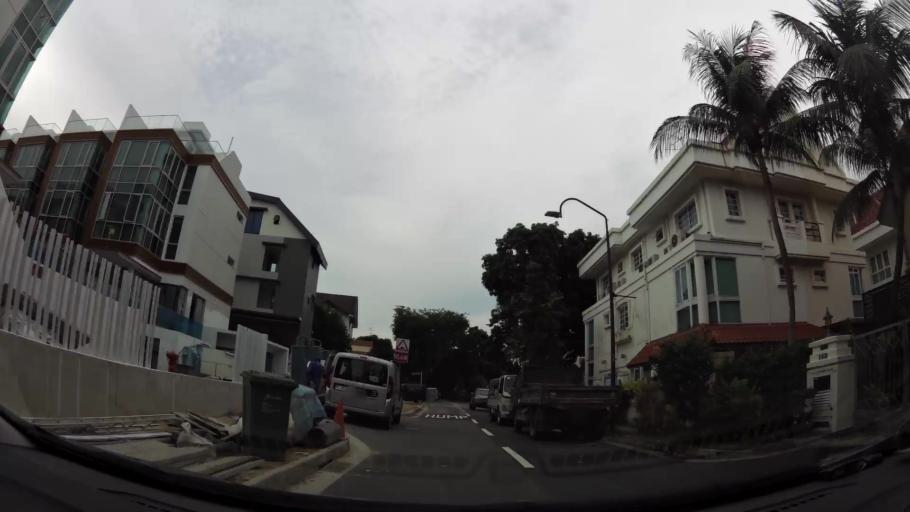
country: SG
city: Singapore
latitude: 1.3622
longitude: 103.8815
